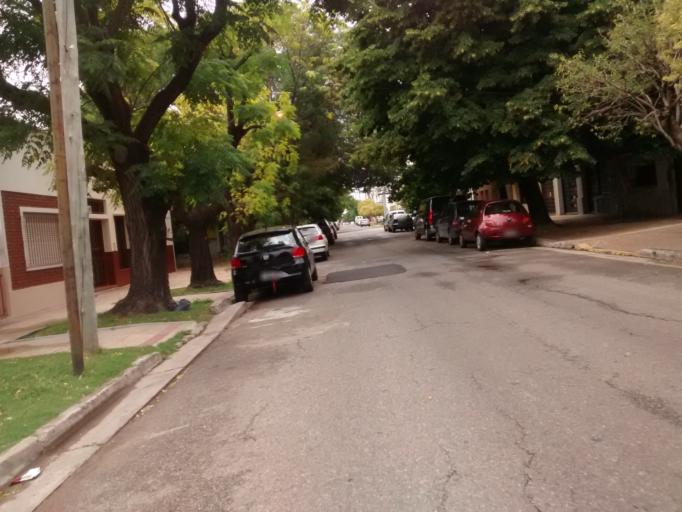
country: AR
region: Buenos Aires
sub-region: Partido de La Plata
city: La Plata
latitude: -34.8993
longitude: -57.9717
